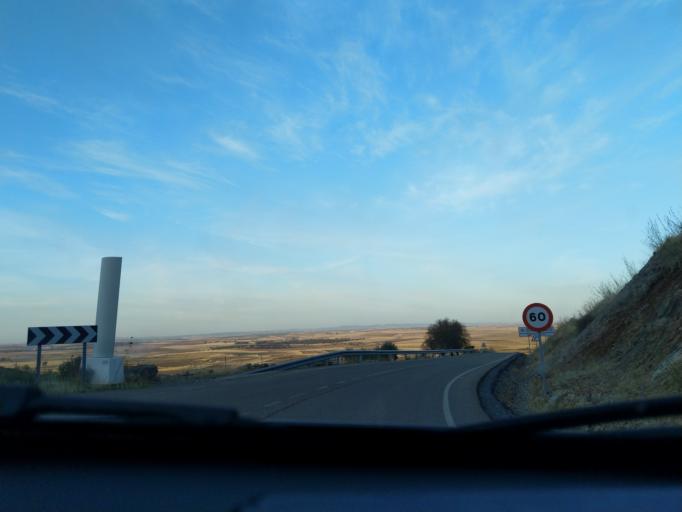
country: ES
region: Extremadura
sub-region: Provincia de Badajoz
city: Reina
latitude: 38.1882
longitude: -5.9493
